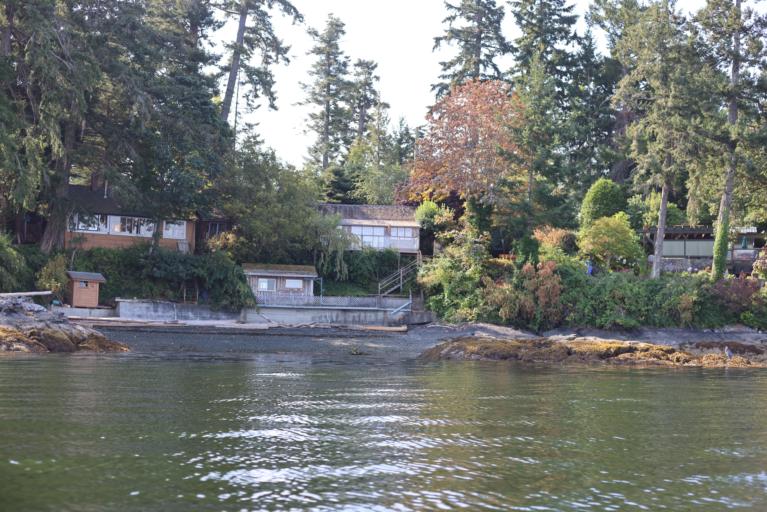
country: CA
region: British Columbia
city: North Saanich
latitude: 48.6778
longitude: -123.4872
